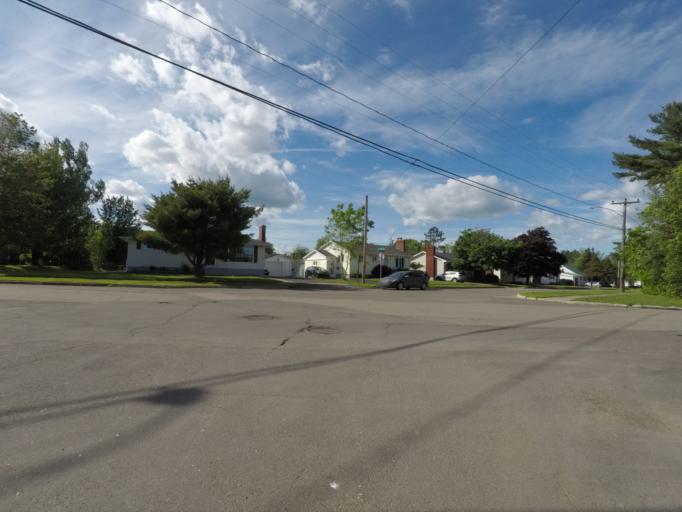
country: CA
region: New Brunswick
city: Moncton
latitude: 46.1035
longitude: -64.8267
